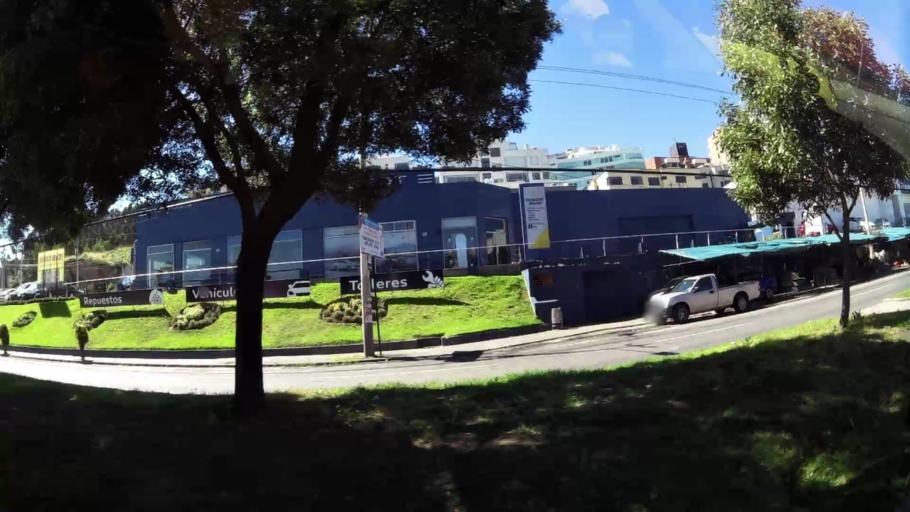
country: EC
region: Pichincha
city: Quito
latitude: -0.1700
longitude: -78.4701
